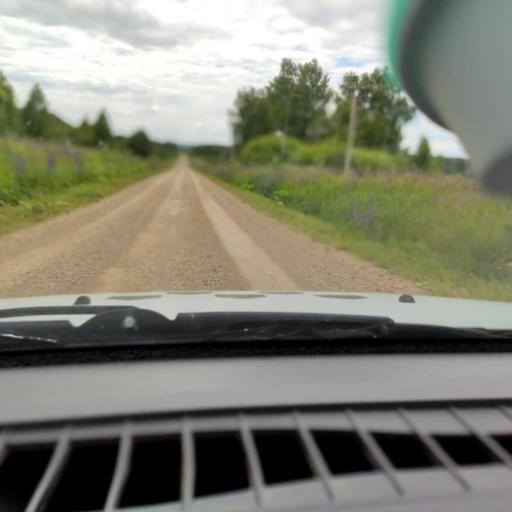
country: RU
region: Perm
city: Suksun
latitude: 57.1944
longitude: 57.5803
